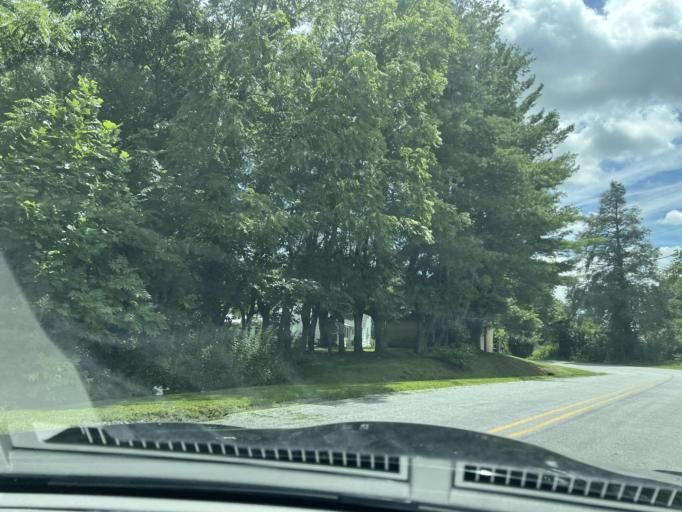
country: US
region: North Carolina
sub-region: Henderson County
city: Fruitland
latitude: 35.3971
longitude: -82.3927
